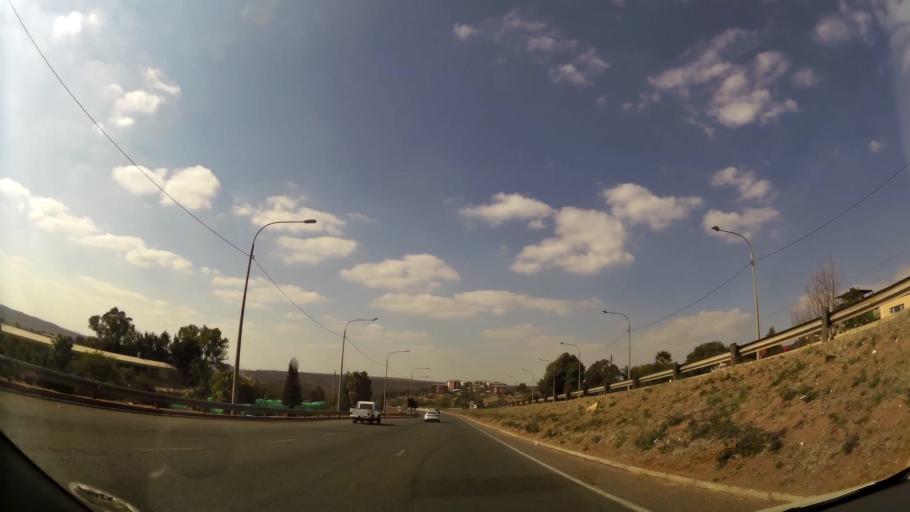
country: ZA
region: Gauteng
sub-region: West Rand District Municipality
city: Krugersdorp
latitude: -26.0773
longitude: 27.7938
